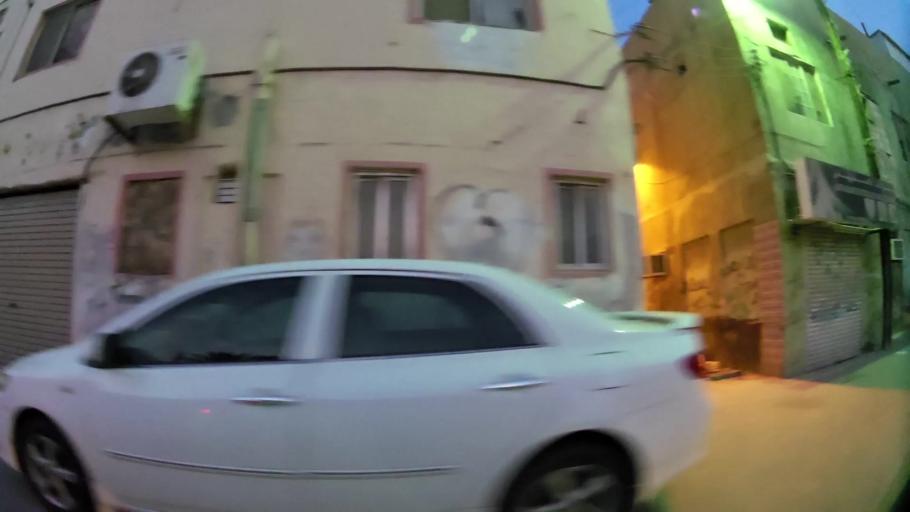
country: BH
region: Manama
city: Jidd Hafs
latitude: 26.2041
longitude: 50.5531
